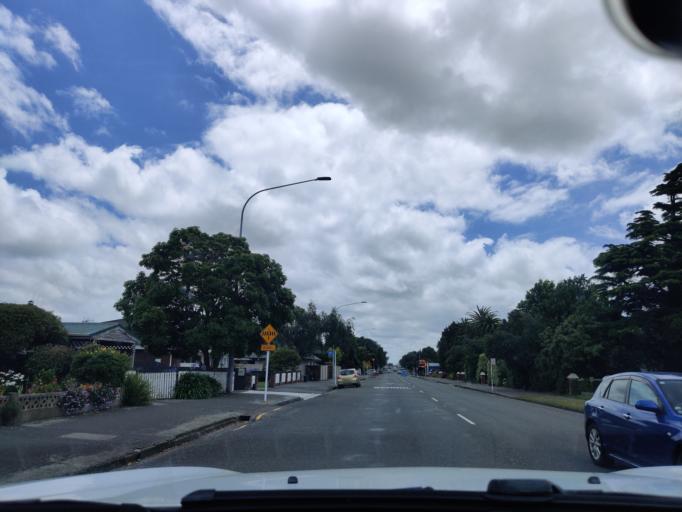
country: NZ
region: Manawatu-Wanganui
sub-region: Palmerston North City
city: Palmerston North
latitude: -40.3580
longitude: 175.6301
